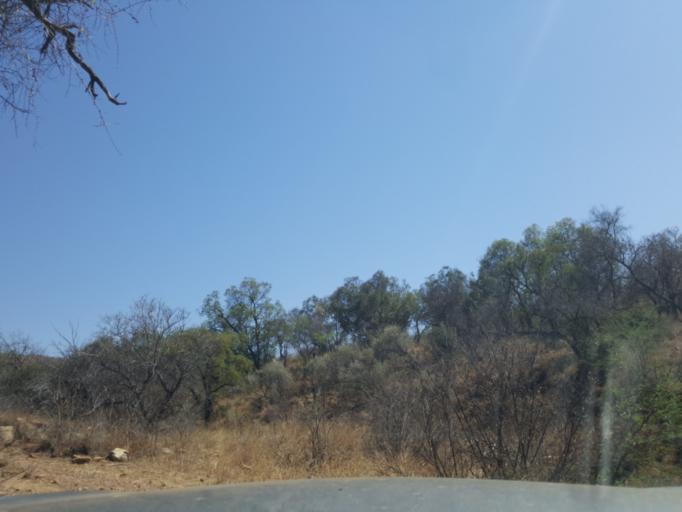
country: BW
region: South East
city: Lobatse
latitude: -25.1492
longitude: 25.6708
